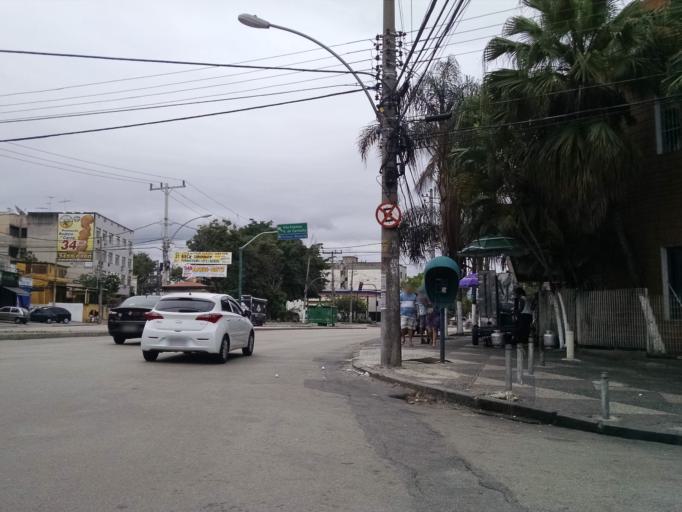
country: BR
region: Rio de Janeiro
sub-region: Duque De Caxias
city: Duque de Caxias
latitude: -22.8395
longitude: -43.3121
